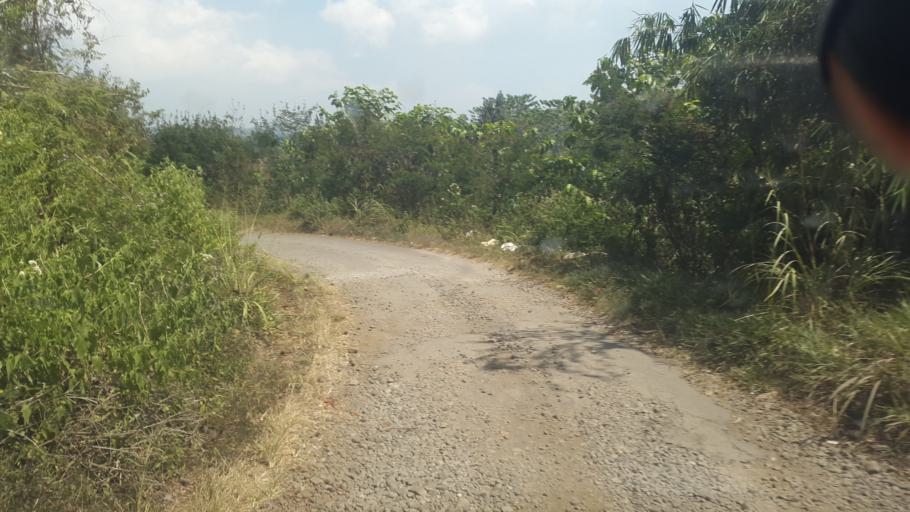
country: ID
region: West Java
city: Pasirreungit
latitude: -7.0086
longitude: 107.0192
